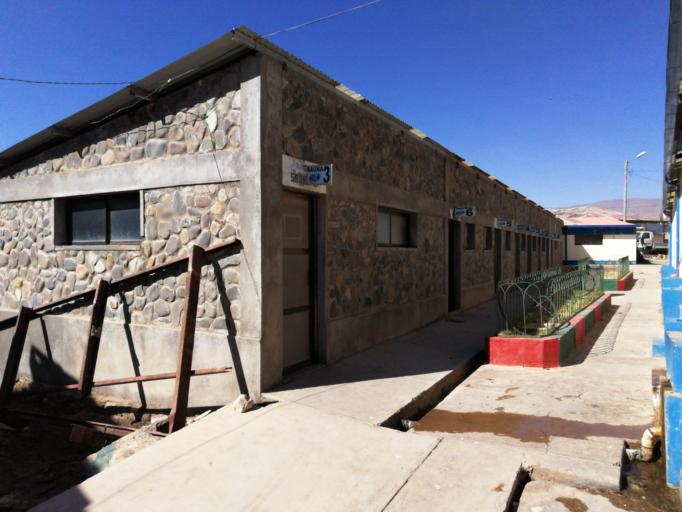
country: BO
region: Potosi
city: Llallagua
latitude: -18.4492
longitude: -66.5483
